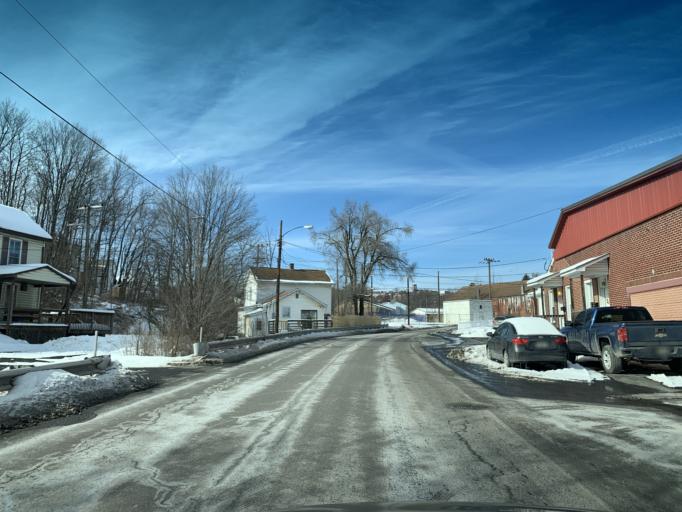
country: US
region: Maryland
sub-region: Allegany County
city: Frostburg
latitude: 39.6505
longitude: -78.9229
